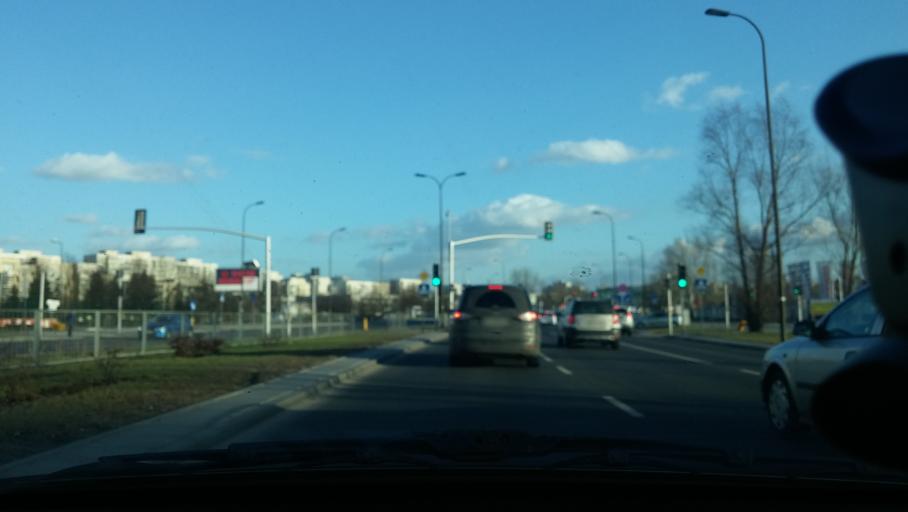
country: PL
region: Masovian Voivodeship
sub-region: Warszawa
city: Ursynow
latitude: 52.1481
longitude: 21.0349
